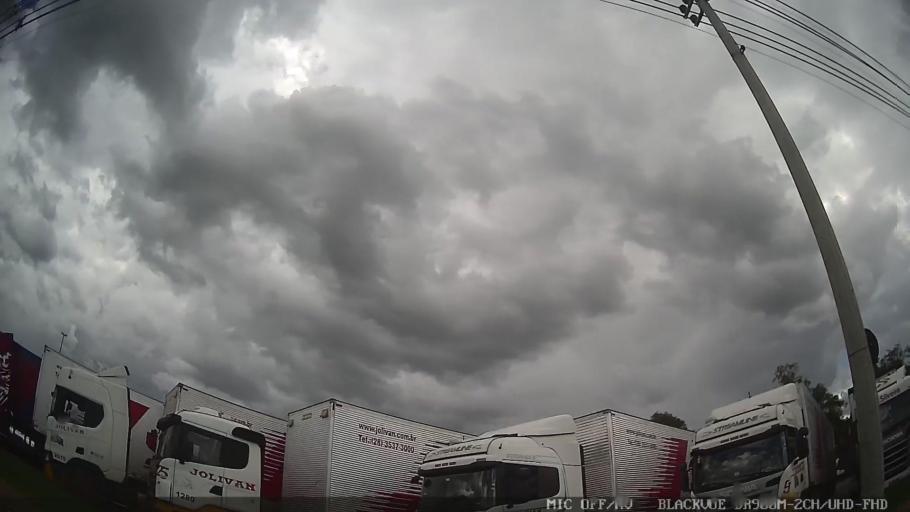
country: BR
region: Sao Paulo
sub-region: Jaguariuna
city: Jaguariuna
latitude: -22.7108
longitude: -47.0103
